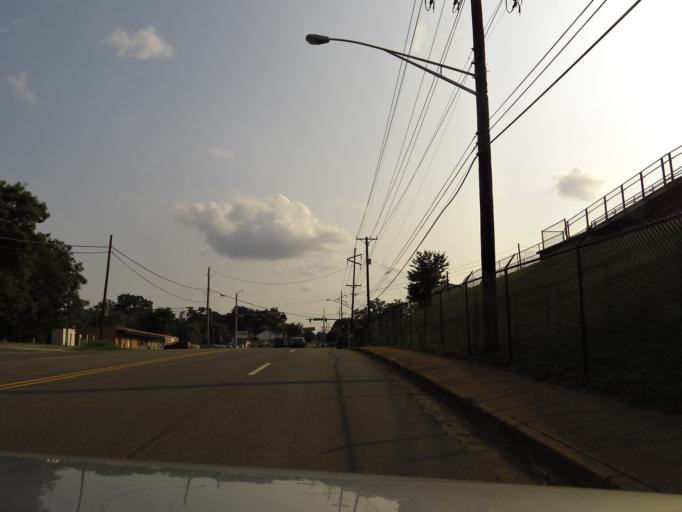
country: US
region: Tennessee
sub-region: Knox County
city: Knoxville
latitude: 35.9921
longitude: -83.9234
